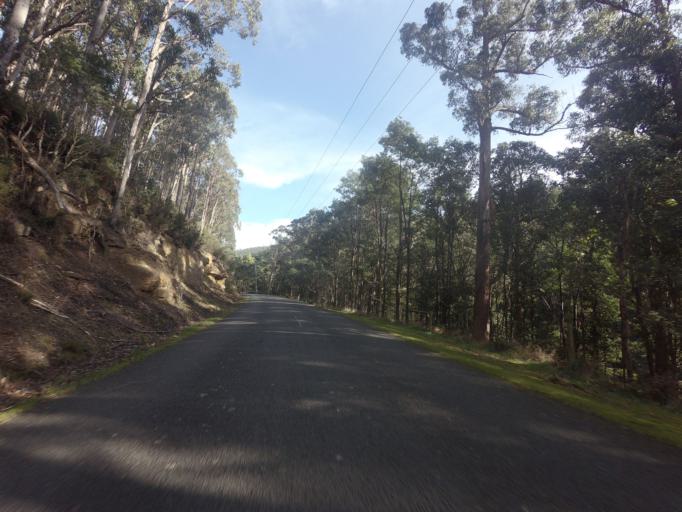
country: AU
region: Tasmania
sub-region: Huon Valley
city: Huonville
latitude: -43.0419
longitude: 147.1271
